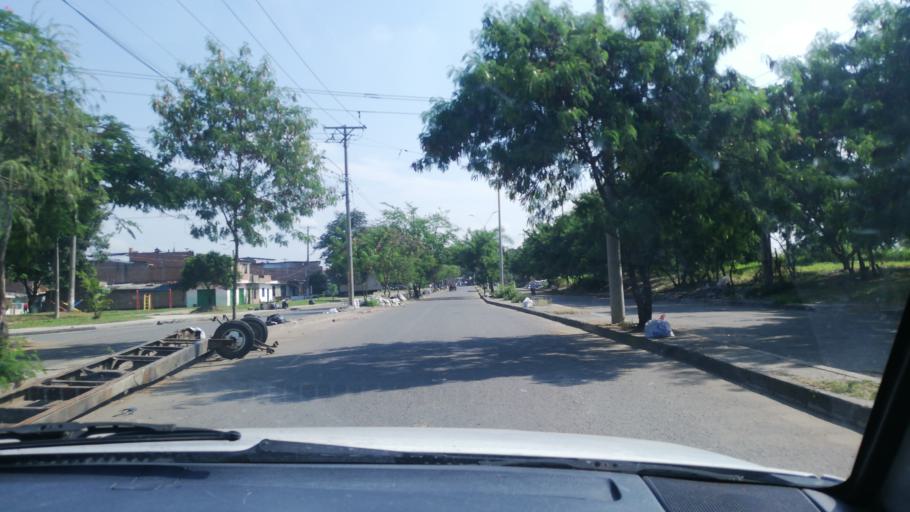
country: CO
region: Valle del Cauca
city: Cali
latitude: 3.4129
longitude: -76.4859
